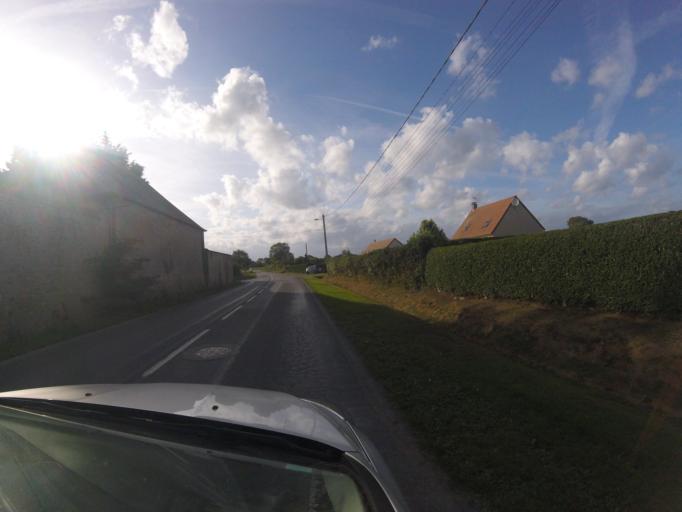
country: FR
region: Lower Normandy
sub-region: Departement du Calvados
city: Port-en-Bessin-Huppain
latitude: 49.3502
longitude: -0.8250
